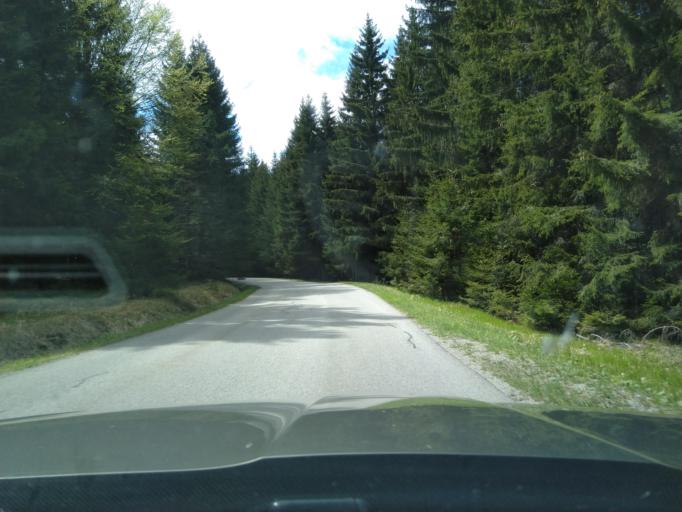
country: CZ
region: Jihocesky
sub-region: Okres Prachatice
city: Borova Lada
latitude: 49.0075
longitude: 13.7081
